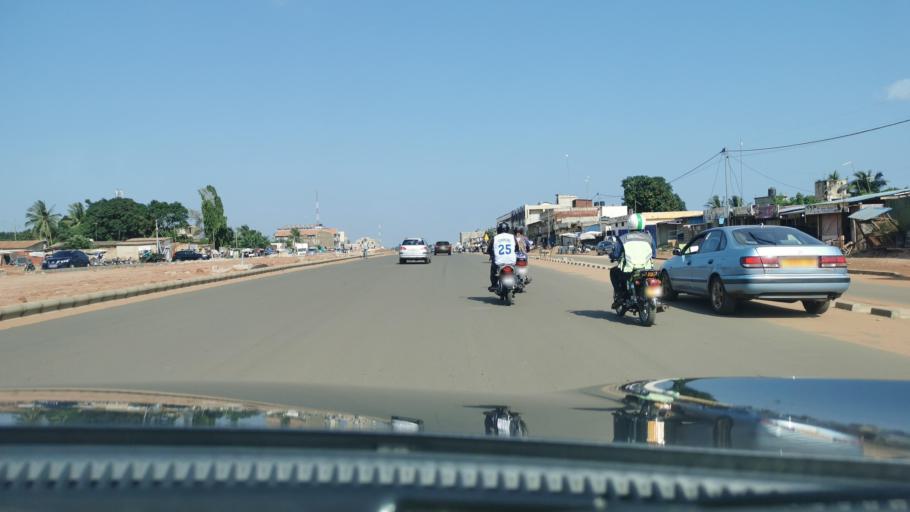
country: TG
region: Maritime
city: Lome
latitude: 6.2043
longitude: 1.1441
